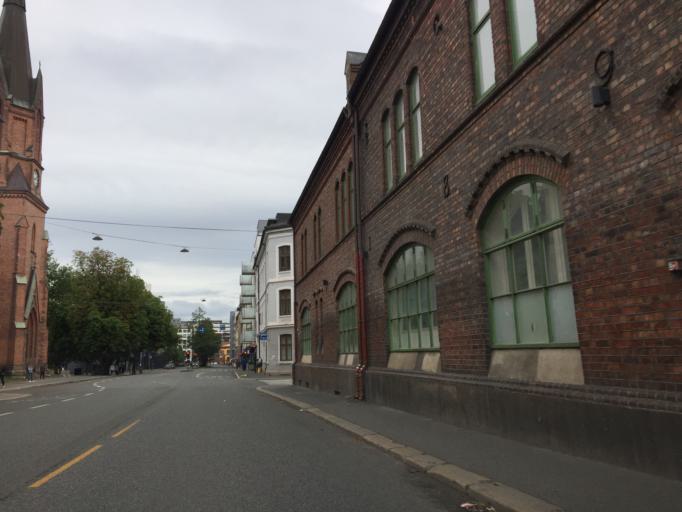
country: NO
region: Oslo
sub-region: Oslo
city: Oslo
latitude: 59.9185
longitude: 10.7529
